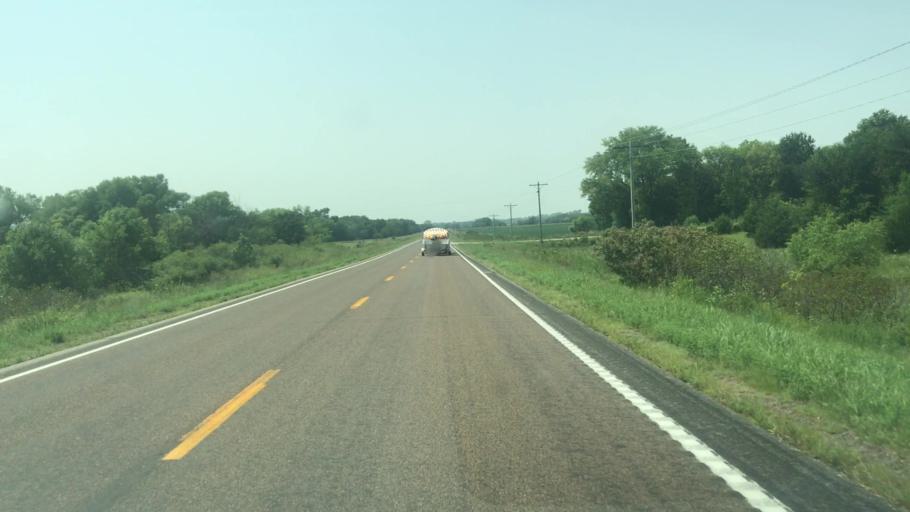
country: US
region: Nebraska
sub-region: Buffalo County
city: Ravenna
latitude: 41.0760
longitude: -98.6699
